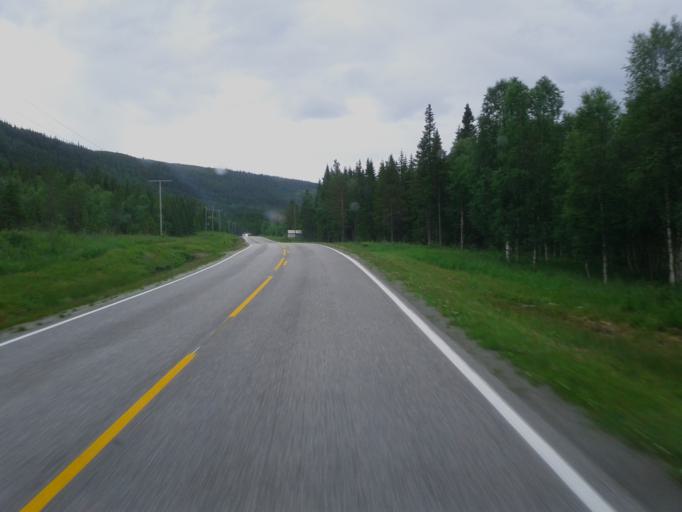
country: NO
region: Nord-Trondelag
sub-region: Namsskogan
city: Namsskogan
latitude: 64.8786
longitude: 13.0671
